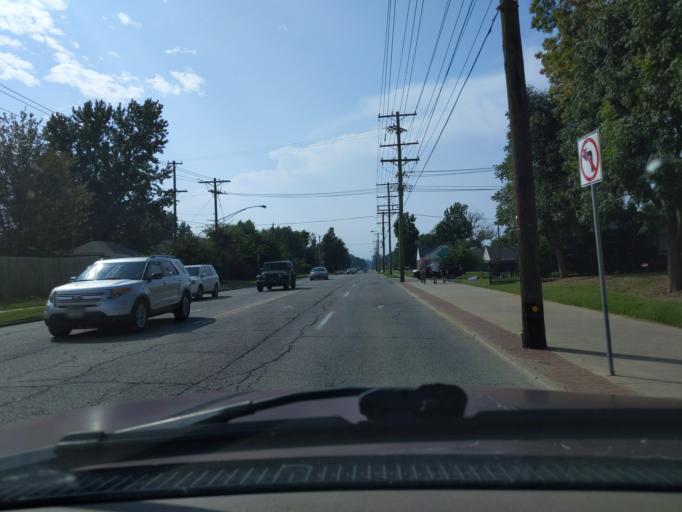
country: US
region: Oklahoma
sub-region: Tulsa County
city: Tulsa
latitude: 36.1333
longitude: -95.9353
